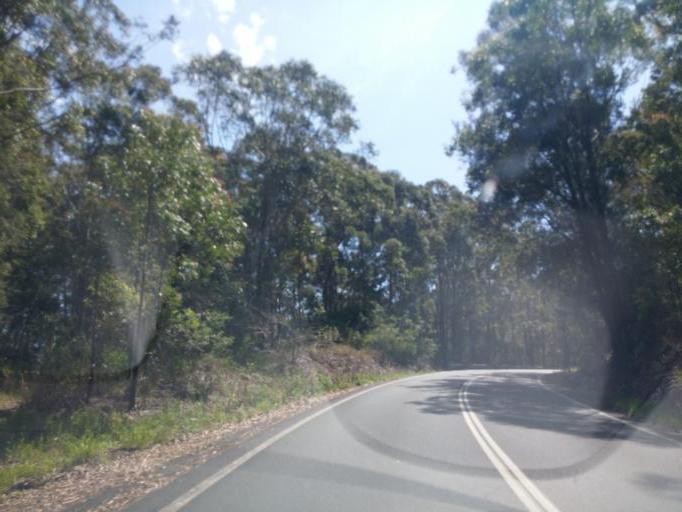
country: AU
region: New South Wales
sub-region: Great Lakes
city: Bulahdelah
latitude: -32.3992
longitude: 152.3032
